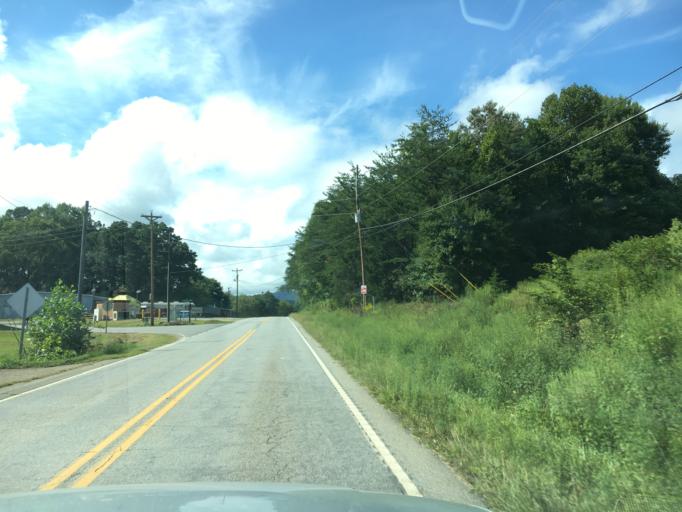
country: US
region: North Carolina
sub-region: Rutherford County
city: Lake Lure
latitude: 35.3737
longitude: -82.1861
